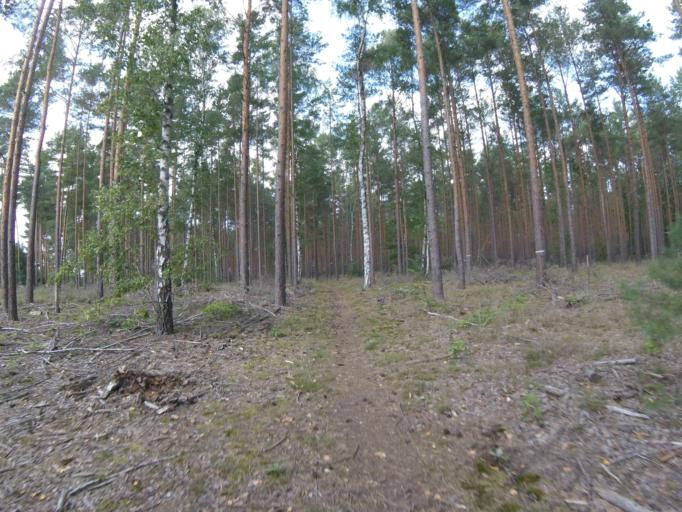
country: DE
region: Brandenburg
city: Bestensee
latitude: 52.2793
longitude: 13.6607
